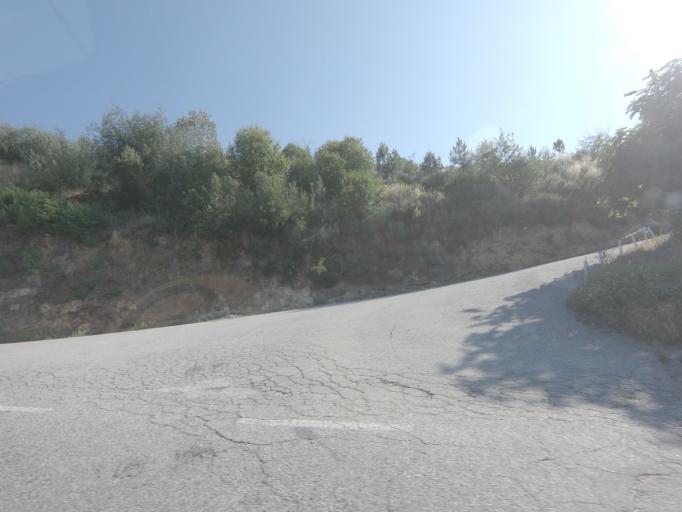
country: PT
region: Viseu
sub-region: Tabuaco
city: Tabuaco
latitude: 41.1139
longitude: -7.5693
